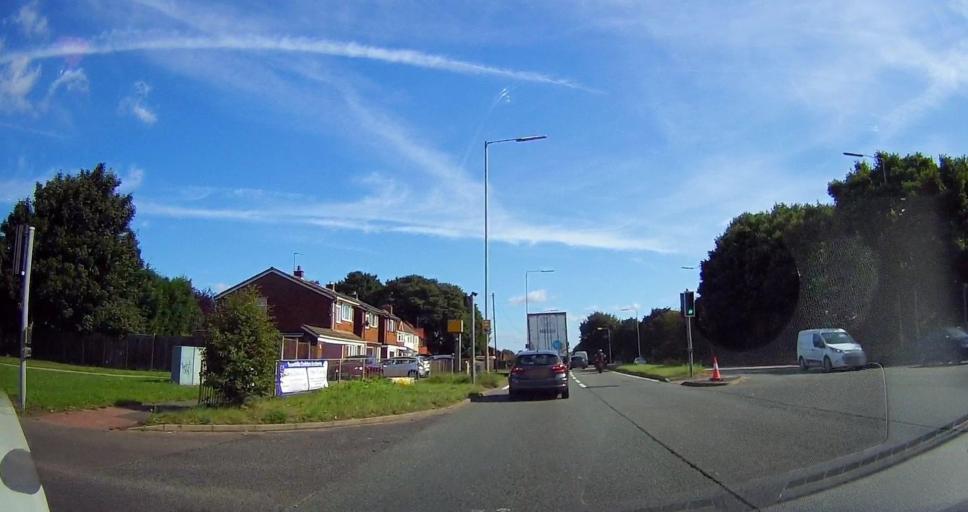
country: GB
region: England
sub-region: Staffordshire
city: Chasetown
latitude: 52.6563
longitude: -1.9387
